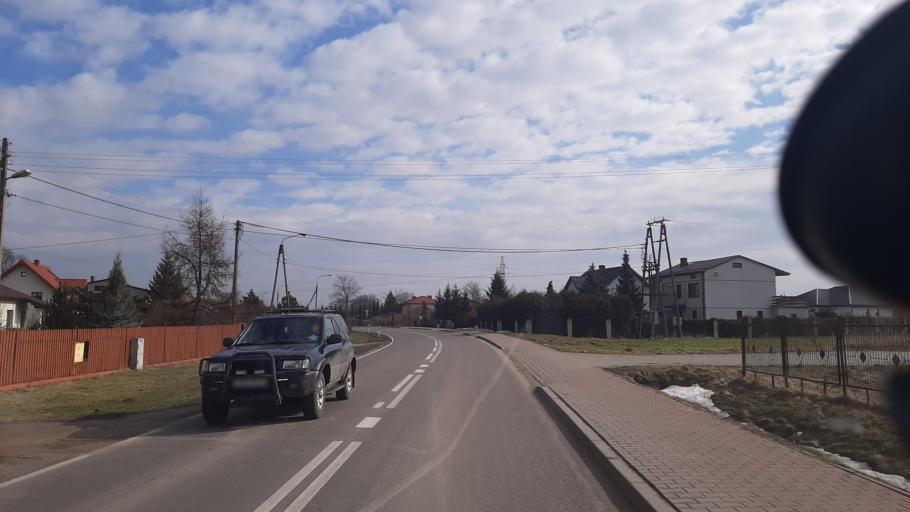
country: PL
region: Lublin Voivodeship
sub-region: Powiat lubelski
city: Niemce
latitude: 51.3591
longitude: 22.6048
